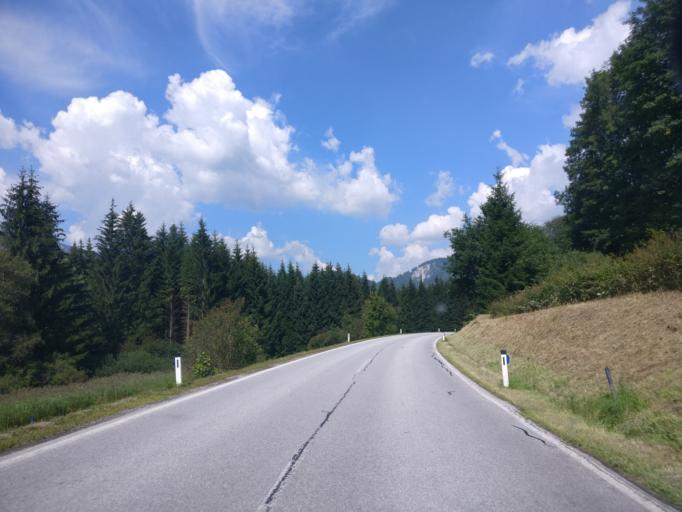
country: AT
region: Styria
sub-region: Politischer Bezirk Liezen
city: Hall bei Admont
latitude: 47.5785
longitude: 14.4870
